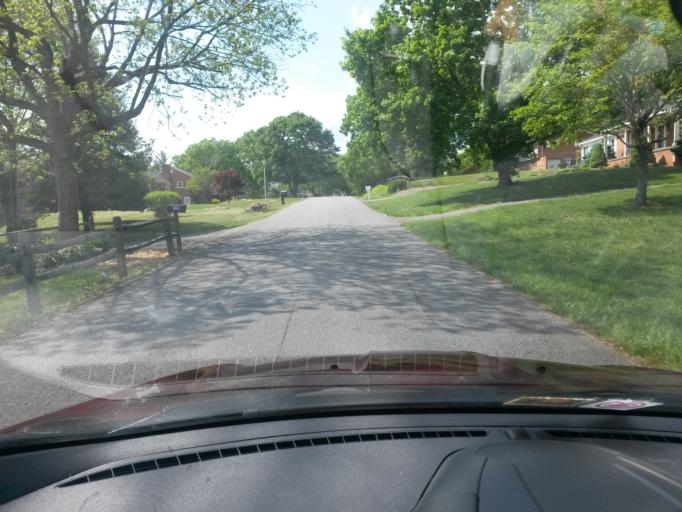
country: US
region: Virginia
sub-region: Campbell County
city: Timberlake
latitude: 37.3475
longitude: -79.2183
